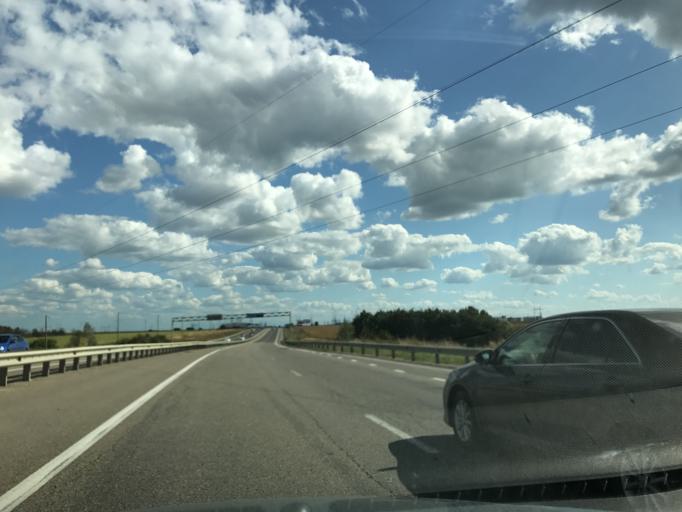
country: RU
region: Adygeya
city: Adygeysk
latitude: 44.8662
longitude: 39.1907
